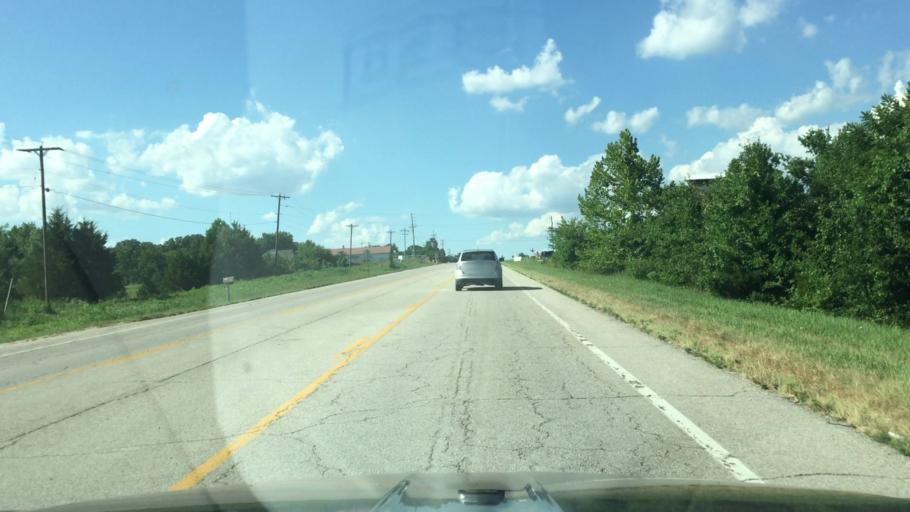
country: US
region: Missouri
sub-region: Miller County
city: Eldon
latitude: 38.3248
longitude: -92.5876
